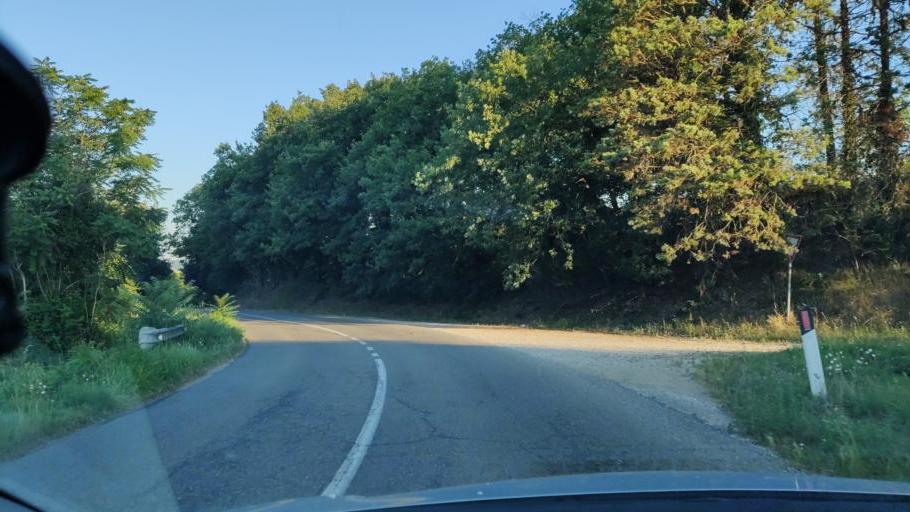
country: IT
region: Umbria
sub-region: Provincia di Terni
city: Attigliano
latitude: 42.5057
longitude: 12.3110
